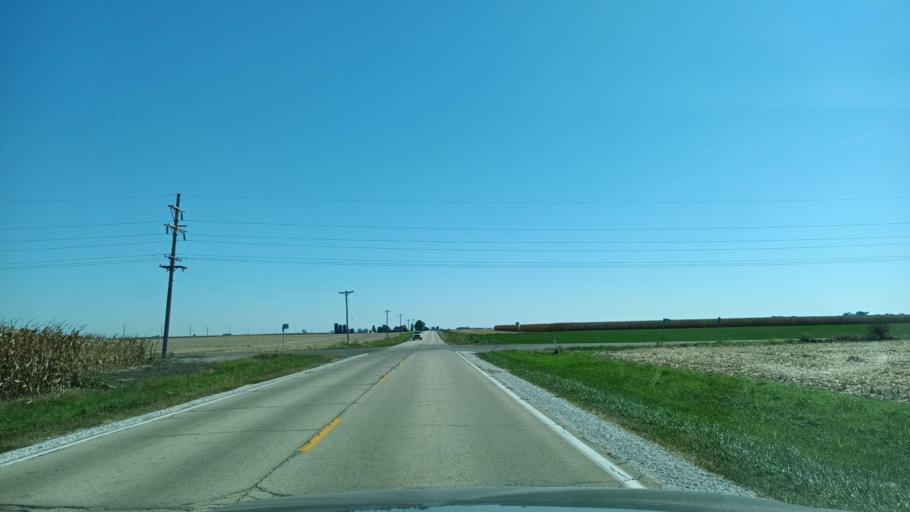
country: US
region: Illinois
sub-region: Peoria County
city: Elmwood
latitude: 40.9022
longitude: -89.9668
